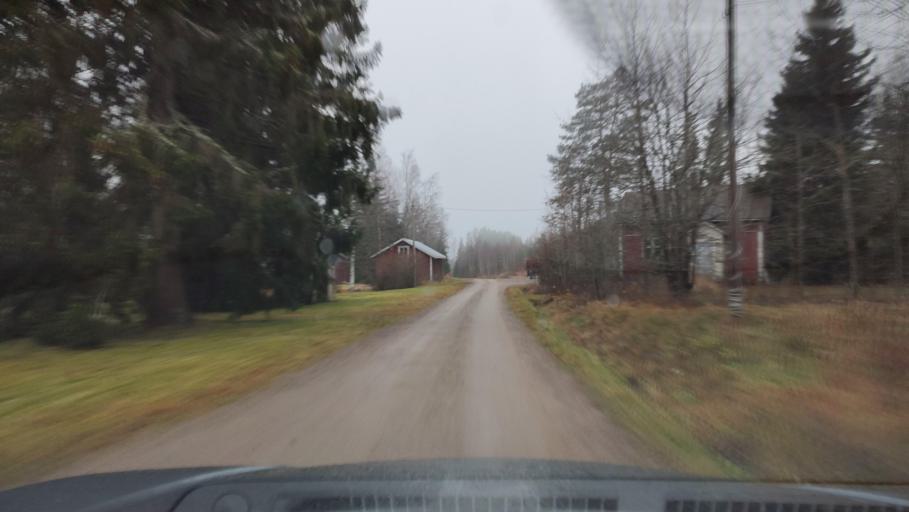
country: FI
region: Southern Ostrobothnia
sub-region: Suupohja
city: Karijoki
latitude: 62.1913
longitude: 21.7784
